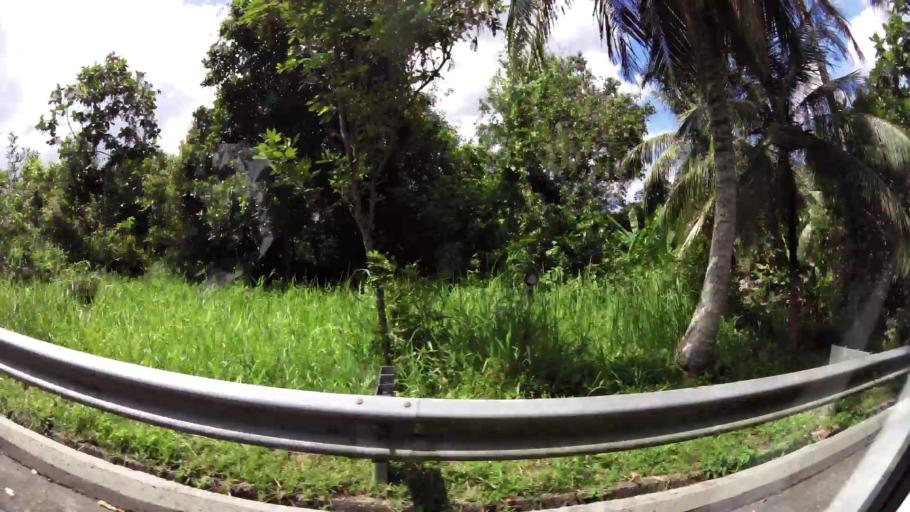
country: BN
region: Brunei and Muara
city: Bandar Seri Begawan
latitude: 4.9444
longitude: 114.9640
